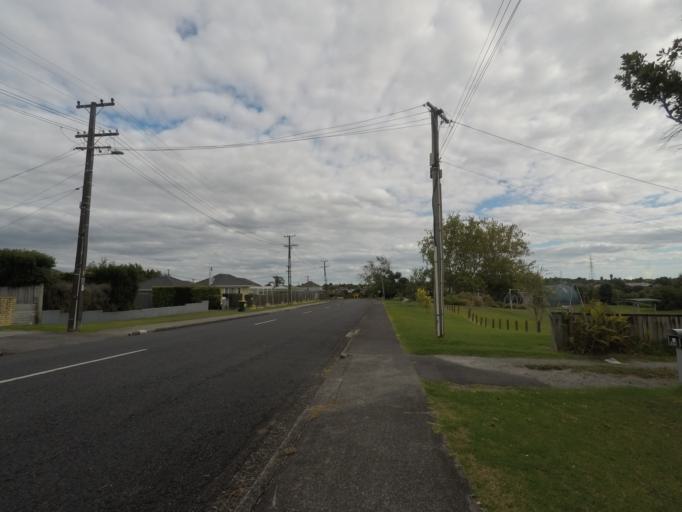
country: NZ
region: Auckland
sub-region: Auckland
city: Papakura
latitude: -37.0589
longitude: 174.9313
